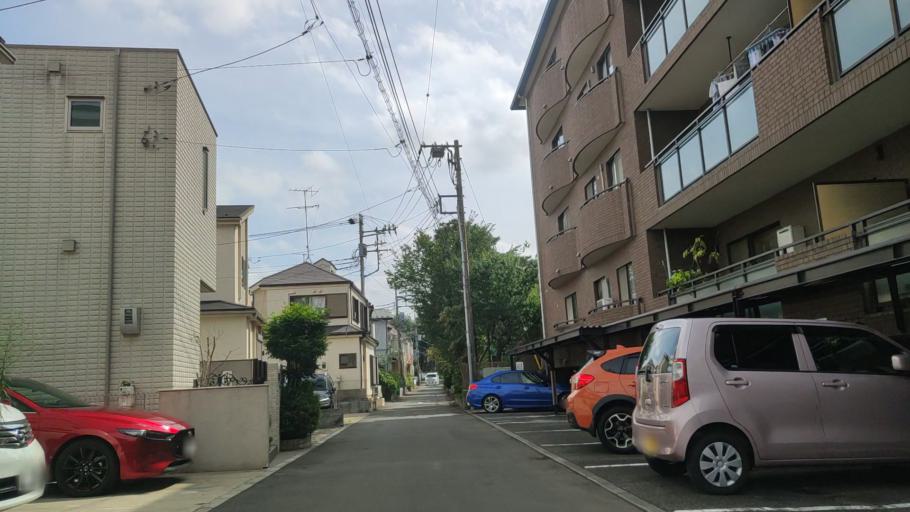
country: JP
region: Kanagawa
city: Minami-rinkan
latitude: 35.5111
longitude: 139.4406
